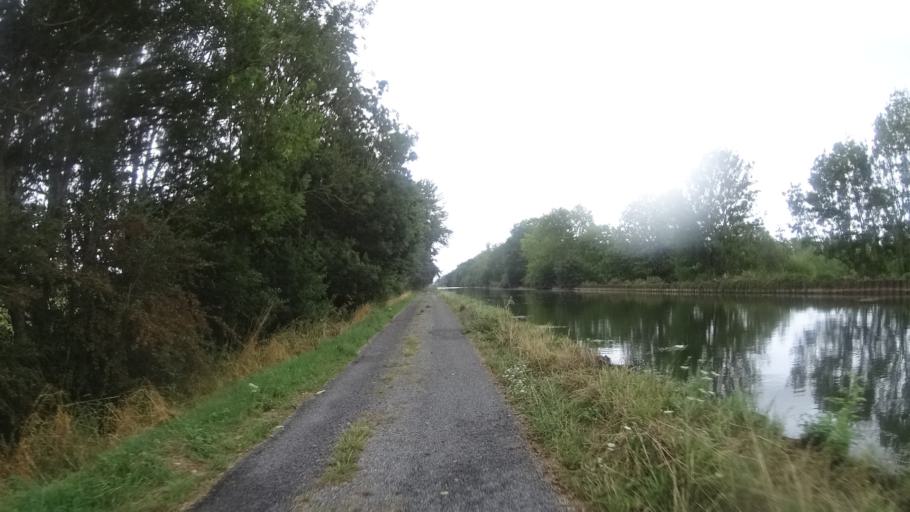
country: FR
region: Picardie
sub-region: Departement de l'Aisne
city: Ribemont
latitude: 49.8113
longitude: 3.4596
